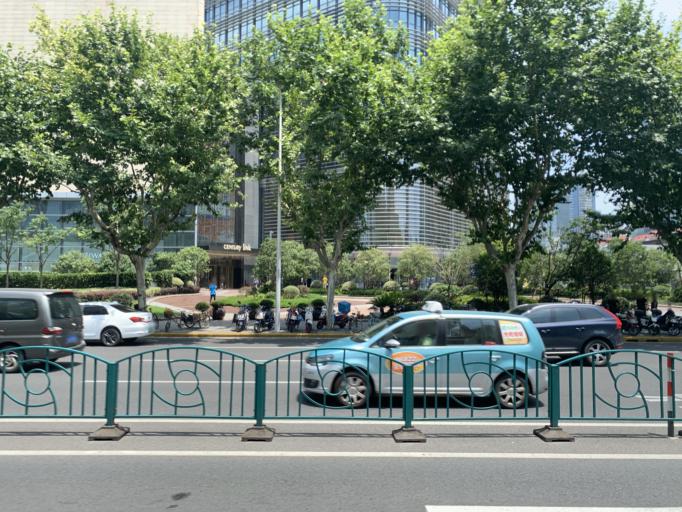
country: CN
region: Shanghai Shi
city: Pudong
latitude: 31.2286
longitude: 121.5220
